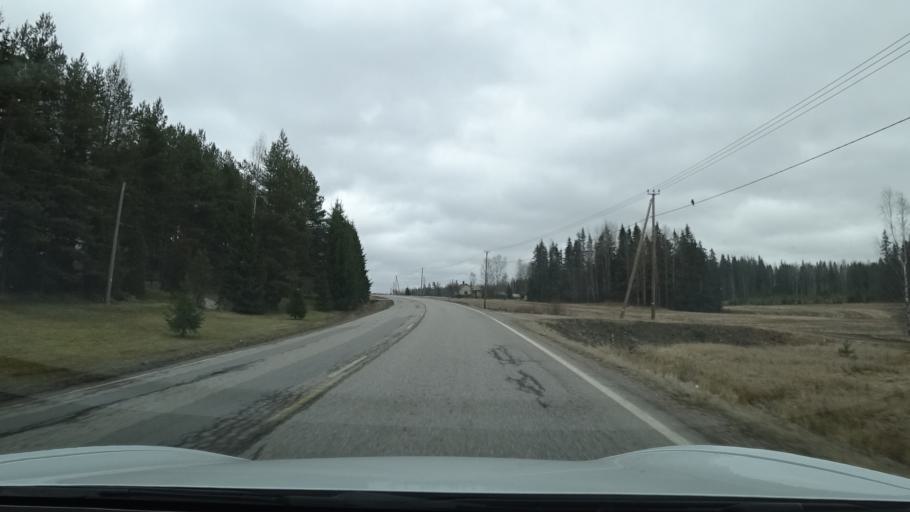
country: FI
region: Uusimaa
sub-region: Porvoo
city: Pukkila
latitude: 60.6434
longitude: 25.6312
